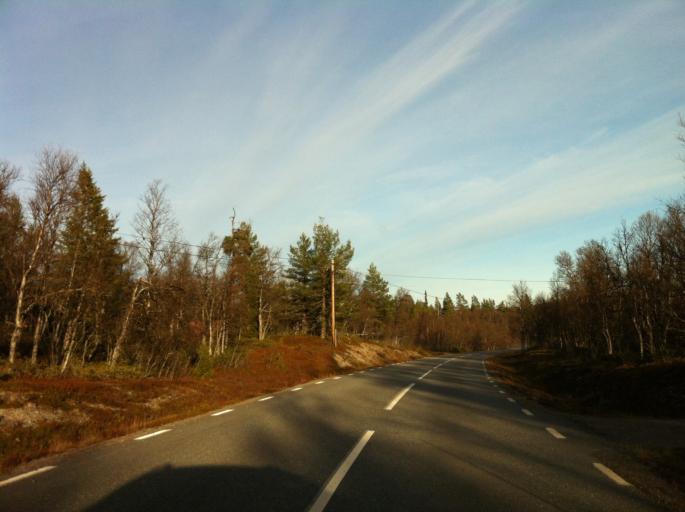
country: NO
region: Hedmark
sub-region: Engerdal
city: Engerdal
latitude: 62.0719
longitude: 12.1946
